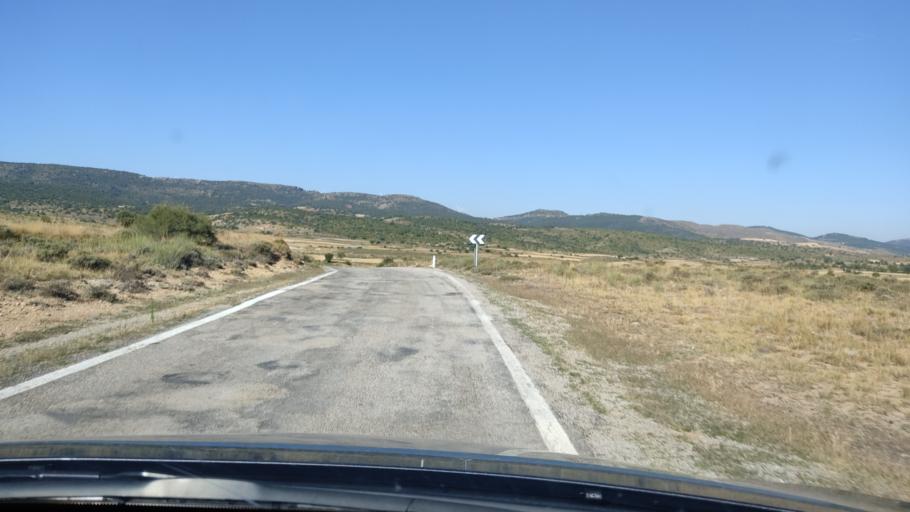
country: ES
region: Aragon
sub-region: Provincia de Teruel
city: Anadon
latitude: 41.0173
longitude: -0.9710
